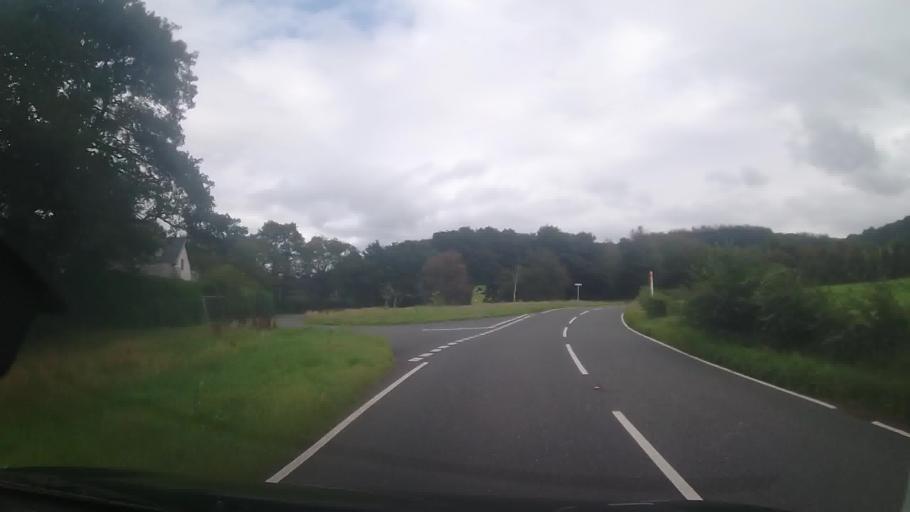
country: GB
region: Wales
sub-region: County of Ceredigion
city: Bow Street
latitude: 52.5144
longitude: -3.9833
